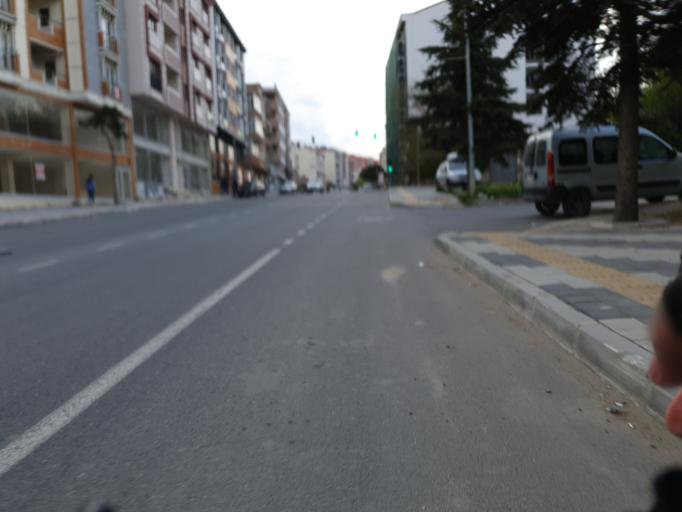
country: TR
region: Tekirdag
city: Saray
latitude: 41.4364
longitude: 27.9191
